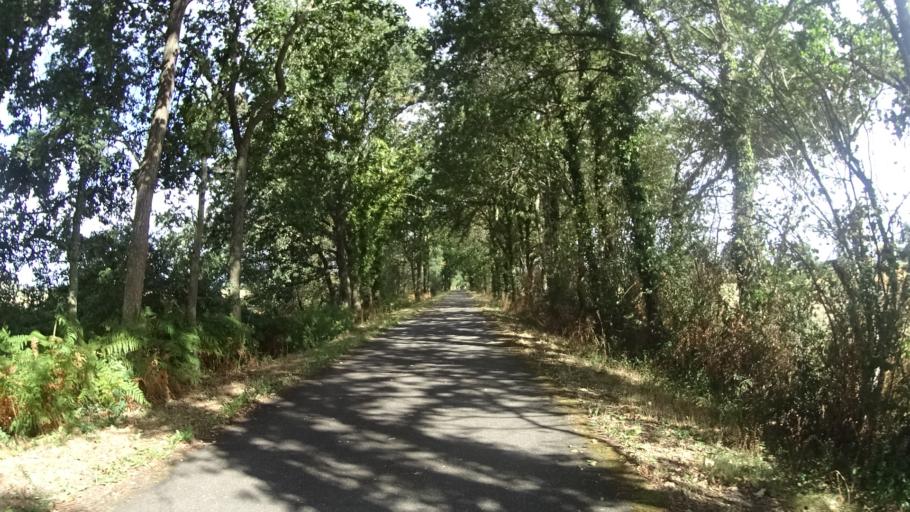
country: FR
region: Bourgogne
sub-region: Departement de Saone-et-Loire
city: Bourbon-Lancy
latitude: 46.6138
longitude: 3.7425
